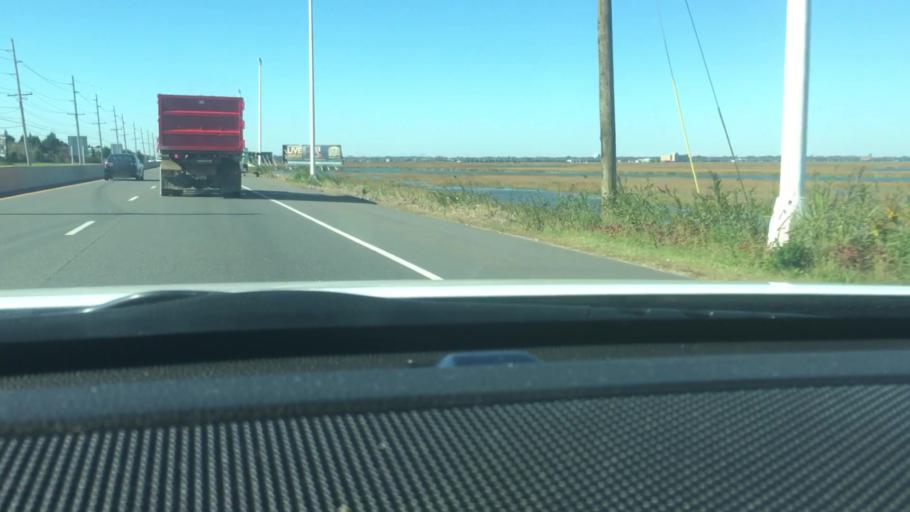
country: US
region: New Jersey
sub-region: Atlantic County
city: Ventnor City
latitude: 39.3870
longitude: -74.4693
